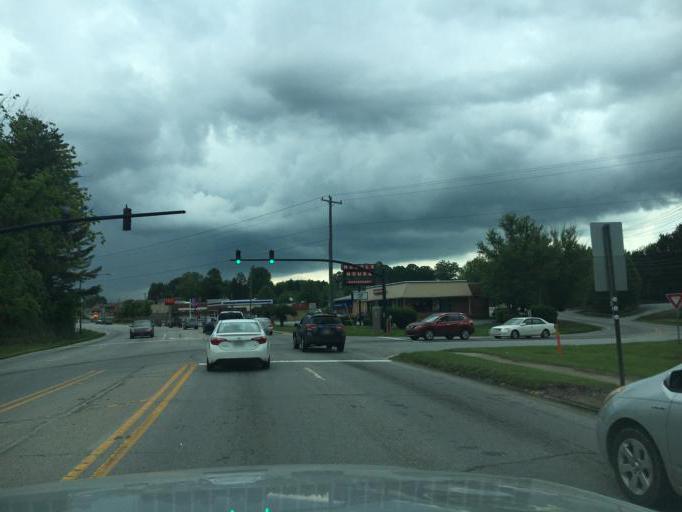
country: US
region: North Carolina
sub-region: Transylvania County
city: Brevard
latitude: 35.2426
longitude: -82.7253
